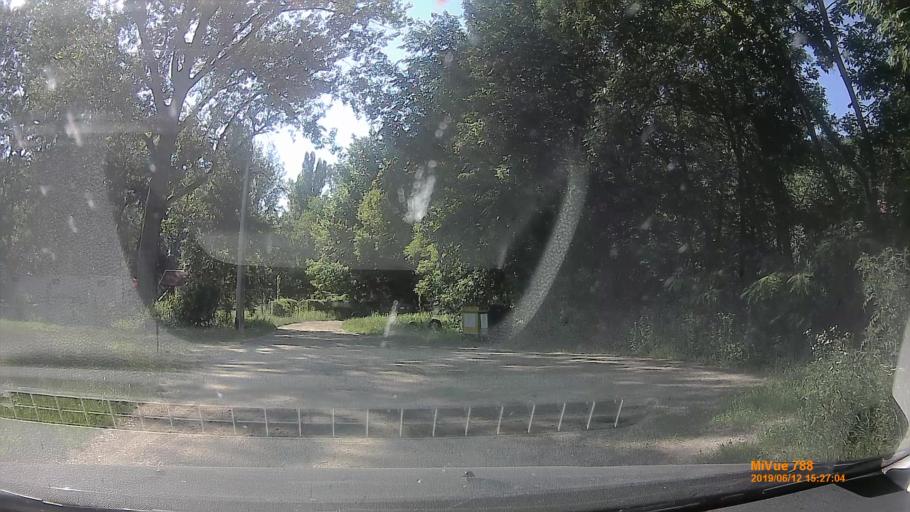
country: HU
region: Csongrad
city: Mako
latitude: 46.1971
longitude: 20.4748
